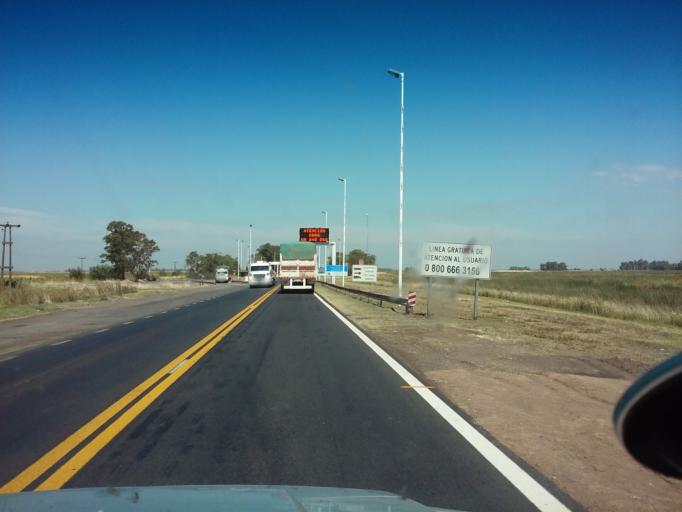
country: AR
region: Buenos Aires
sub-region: Partido de Nueve de Julio
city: Nueve de Julio
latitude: -35.3586
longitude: -60.7007
